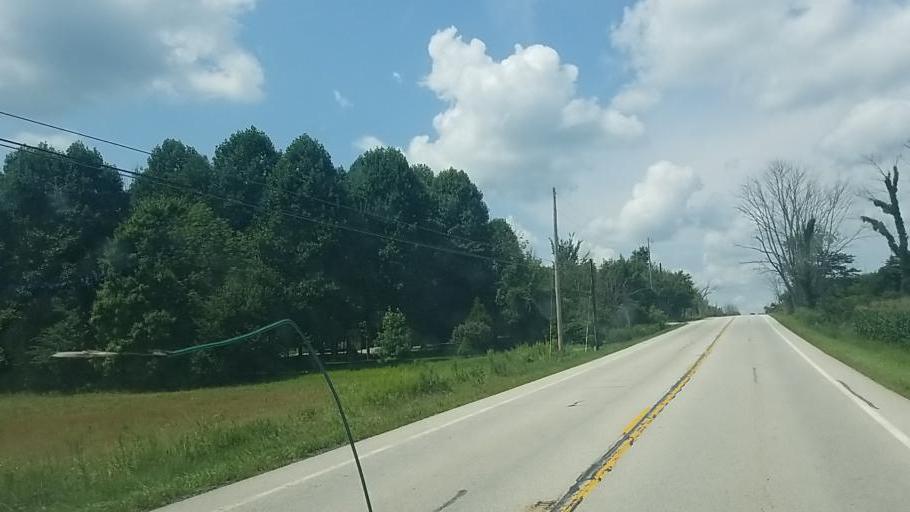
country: US
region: Ohio
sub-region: Medina County
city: Lodi
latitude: 41.0266
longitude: -82.0647
